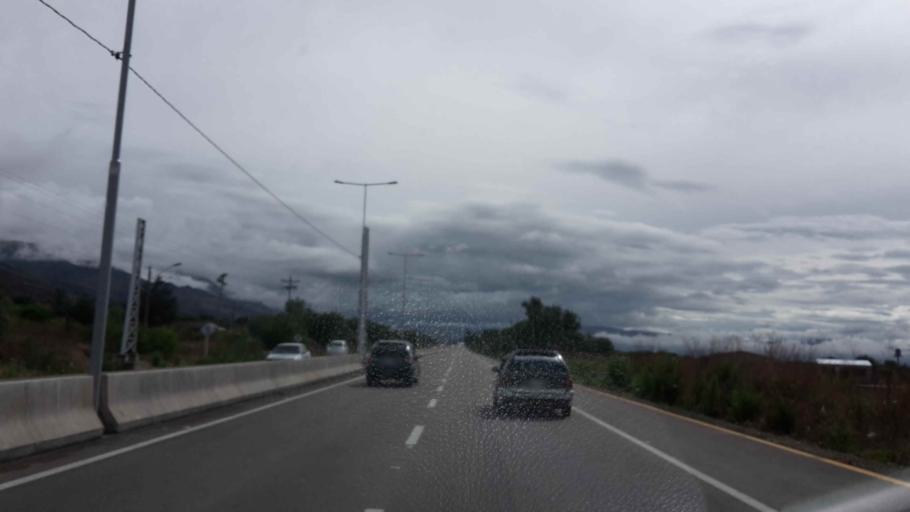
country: BO
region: Cochabamba
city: Tarata
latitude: -17.5443
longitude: -66.0046
